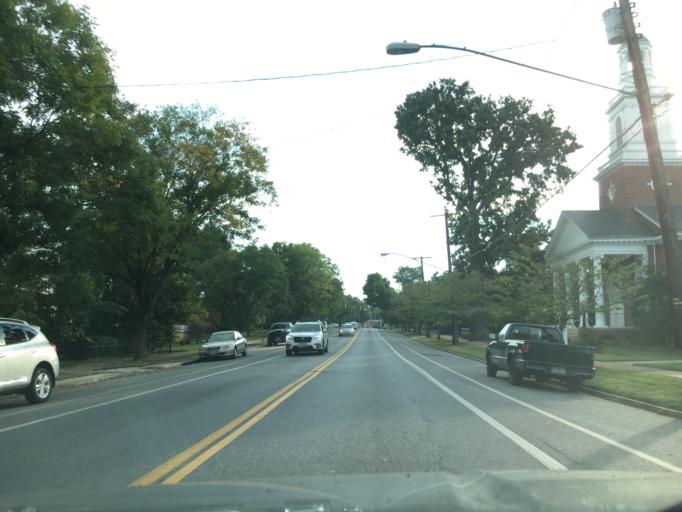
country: US
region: Virginia
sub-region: City of Lynchburg
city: Lynchburg
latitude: 37.4365
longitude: -79.1675
